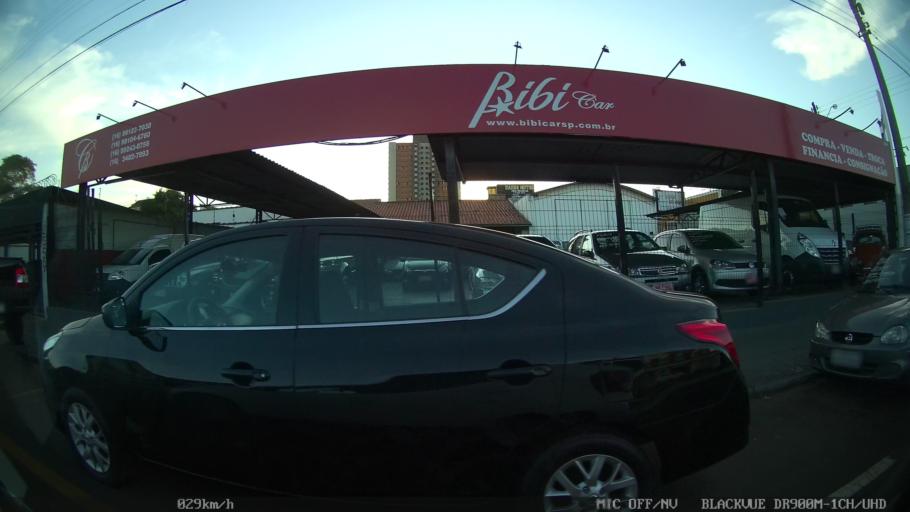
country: BR
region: Sao Paulo
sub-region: Franca
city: Franca
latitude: -20.5300
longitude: -47.4038
